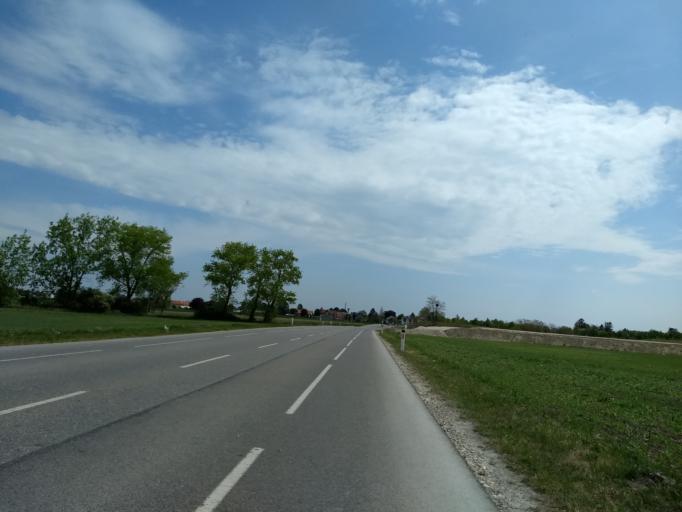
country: AT
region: Lower Austria
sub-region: Politischer Bezirk Ganserndorf
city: Gross-Enzersdorf
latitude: 48.2330
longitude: 16.5131
